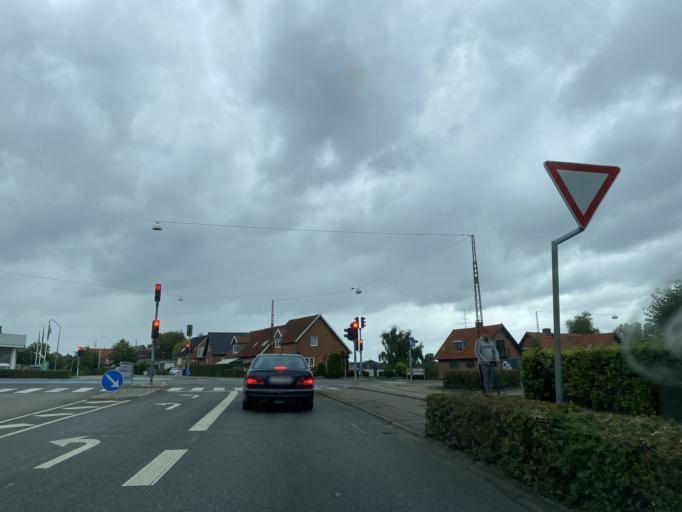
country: DK
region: South Denmark
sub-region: Sonderborg Kommune
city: Sonderborg
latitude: 54.9163
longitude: 9.8016
